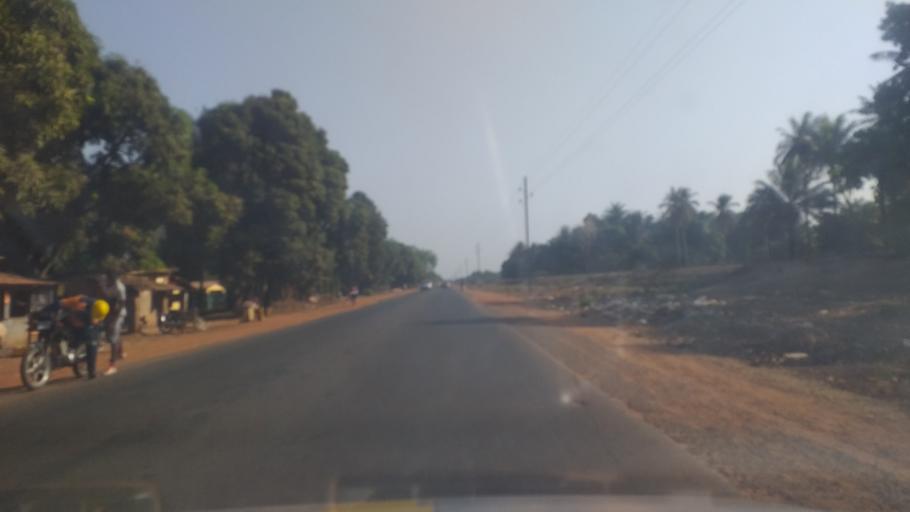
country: GN
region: Boke
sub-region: Boke Prefecture
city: Kamsar
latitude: 10.7159
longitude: -14.5220
